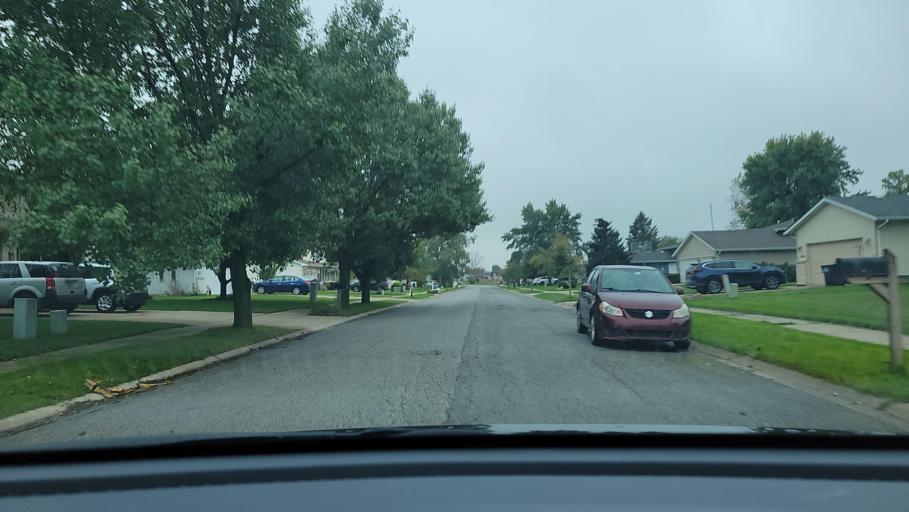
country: US
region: Indiana
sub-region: Porter County
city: Portage
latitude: 41.5455
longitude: -87.1930
